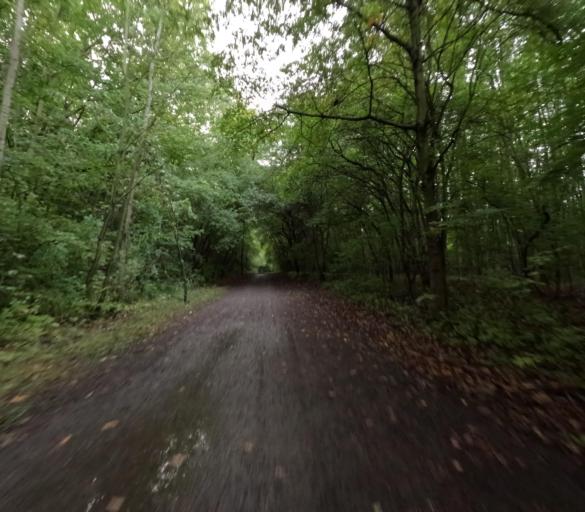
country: DE
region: Saxony
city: Markranstadt
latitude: 51.2914
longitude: 12.2289
